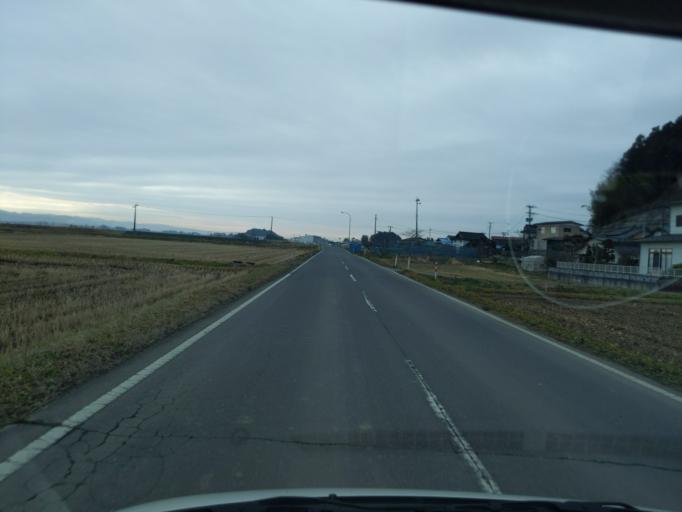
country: JP
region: Iwate
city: Ichinoseki
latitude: 38.7462
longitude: 141.2245
